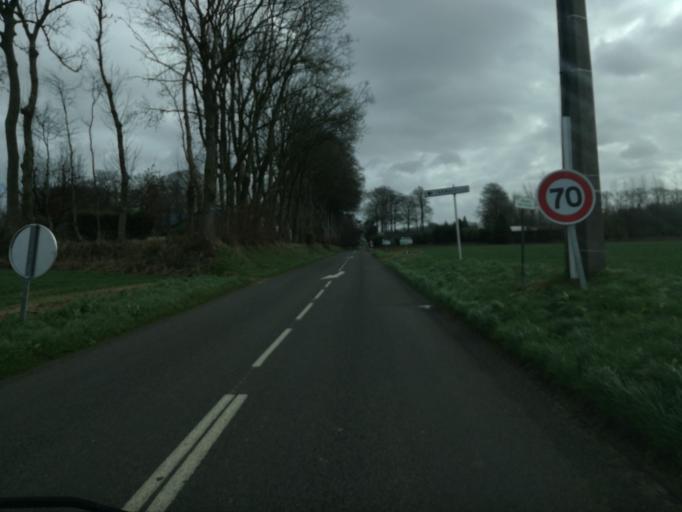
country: FR
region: Haute-Normandie
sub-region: Departement de la Seine-Maritime
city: Yebleron
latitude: 49.6579
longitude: 0.5206
